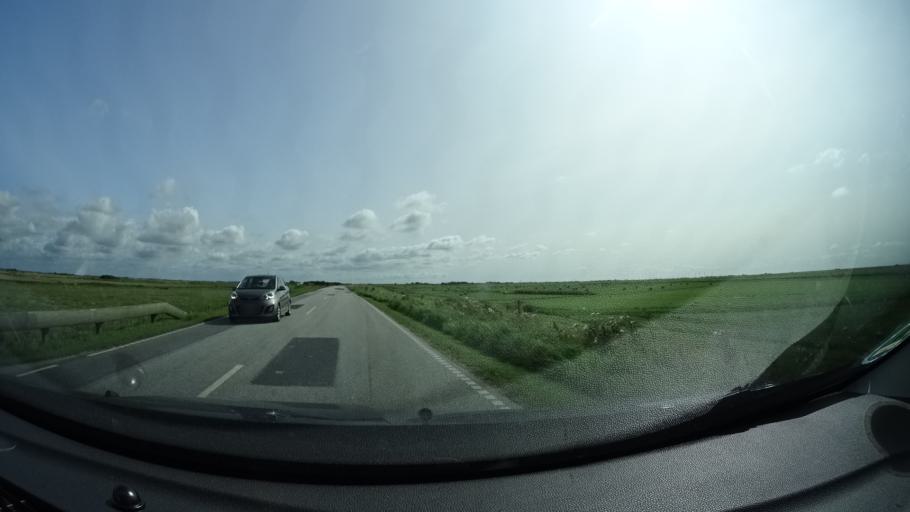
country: DE
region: Schleswig-Holstein
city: Rodenas
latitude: 54.9456
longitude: 8.7077
